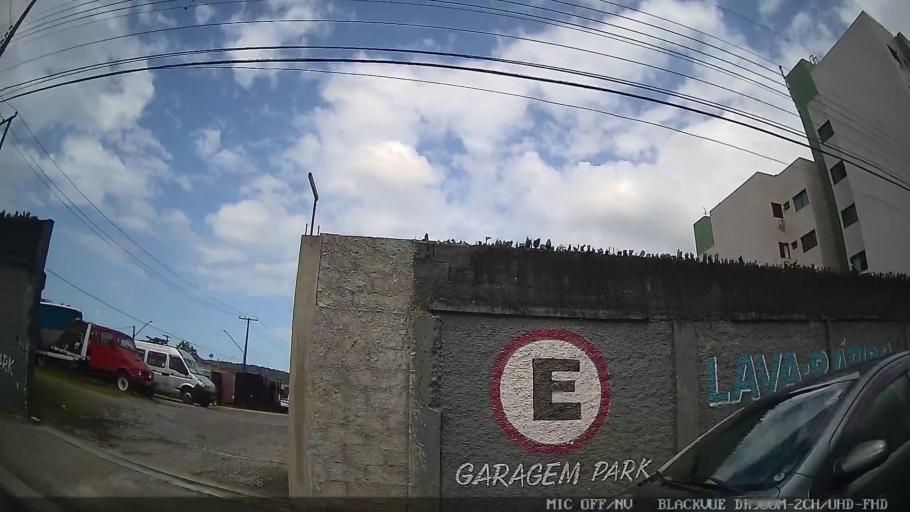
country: BR
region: Sao Paulo
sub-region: Guaruja
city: Guaruja
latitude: -23.9909
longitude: -46.2890
